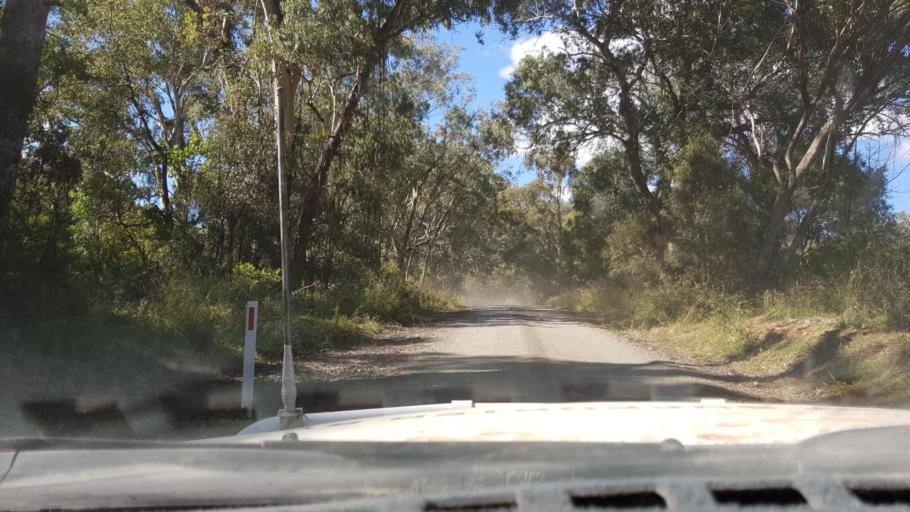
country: AU
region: New South Wales
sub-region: Tamworth Municipality
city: Manilla
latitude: -30.4807
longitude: 150.7657
